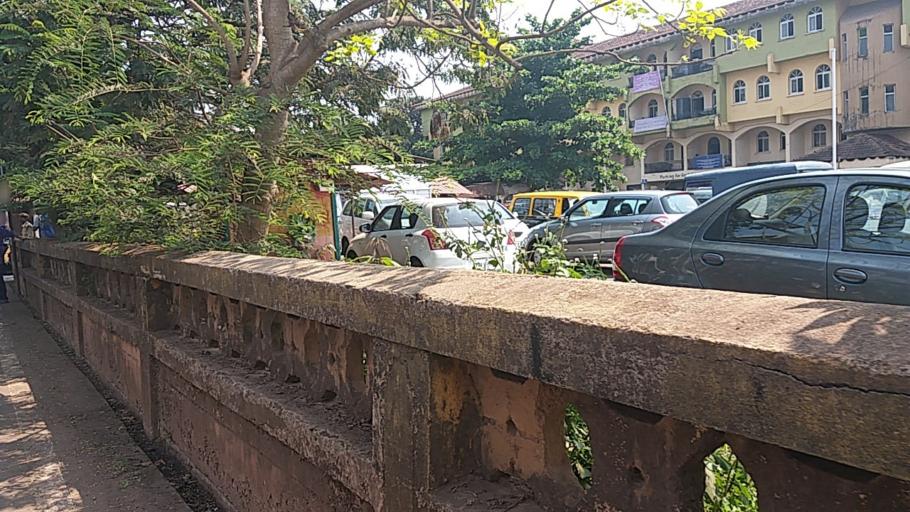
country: IN
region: Goa
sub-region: North Goa
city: Mapuca
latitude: 15.5876
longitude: 73.8134
